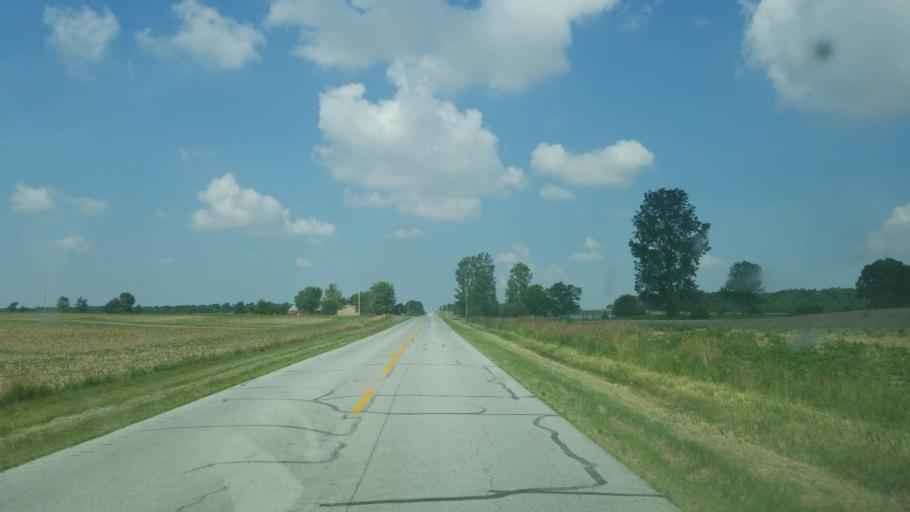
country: US
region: Ohio
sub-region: Shelby County
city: Jackson Center
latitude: 40.5715
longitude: -84.0298
